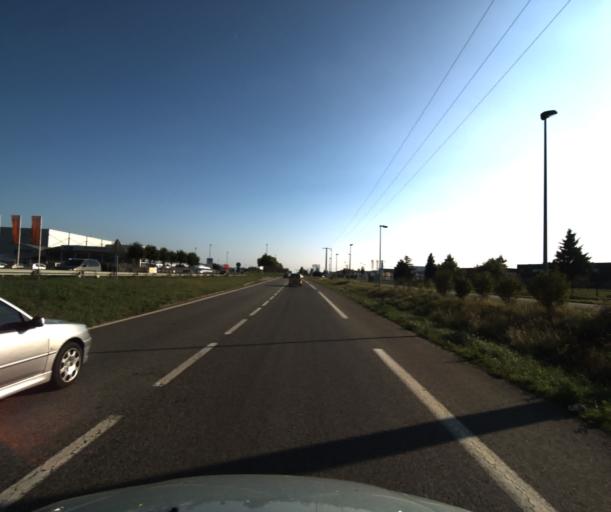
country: FR
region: Midi-Pyrenees
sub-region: Departement de la Haute-Garonne
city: Saubens
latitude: 43.4928
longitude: 1.3436
